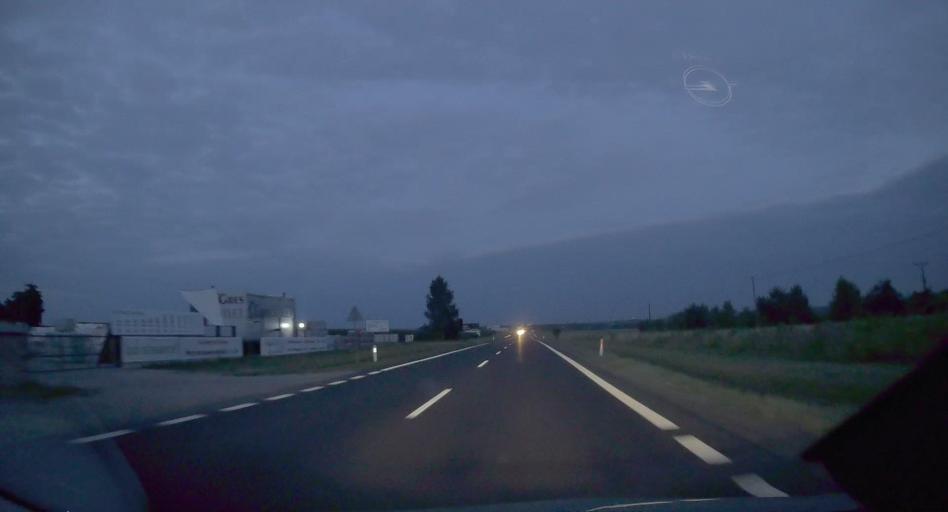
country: PL
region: Silesian Voivodeship
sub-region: Powiat klobucki
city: Klobuck
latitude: 50.8949
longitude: 18.9541
